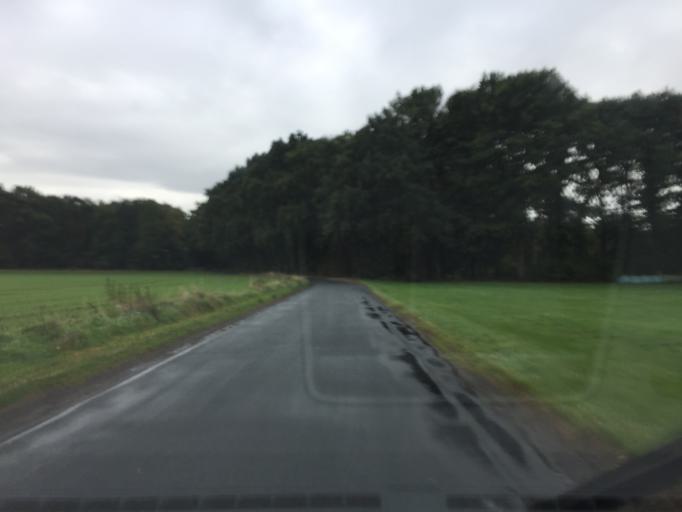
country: DE
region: Lower Saxony
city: Liebenau
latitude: 52.6376
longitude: 9.1010
